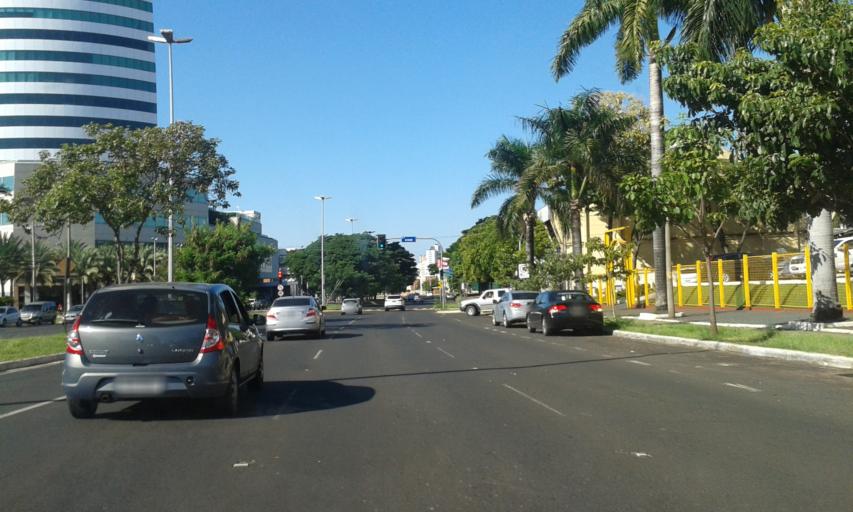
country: BR
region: Minas Gerais
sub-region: Uberlandia
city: Uberlandia
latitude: -18.9070
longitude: -48.2616
